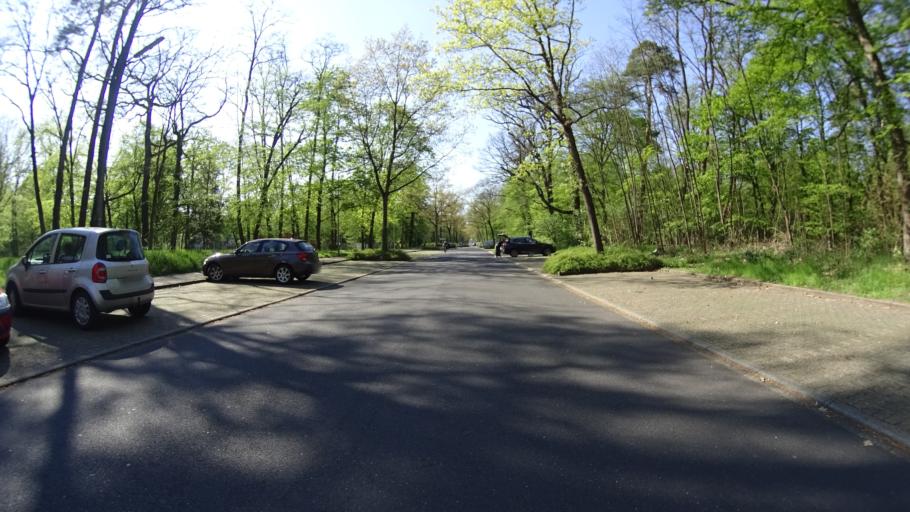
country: DE
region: Baden-Wuerttemberg
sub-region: Karlsruhe Region
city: Karlsruhe
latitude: 49.0170
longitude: 8.3951
